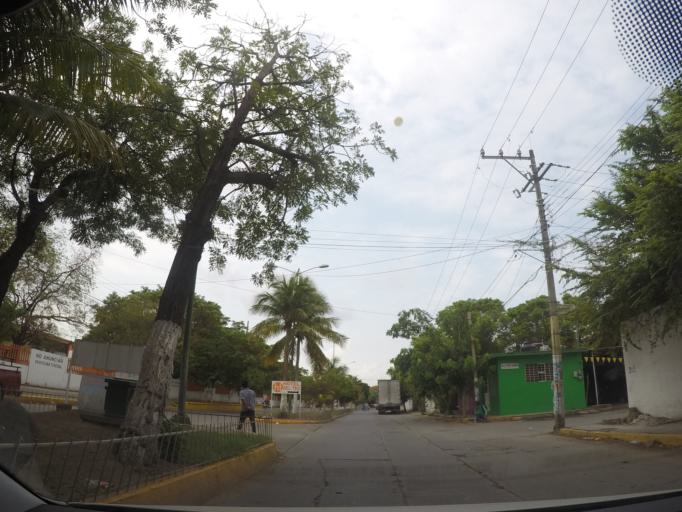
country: MX
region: Oaxaca
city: Juchitan de Zaragoza
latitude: 16.4450
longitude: -95.0170
